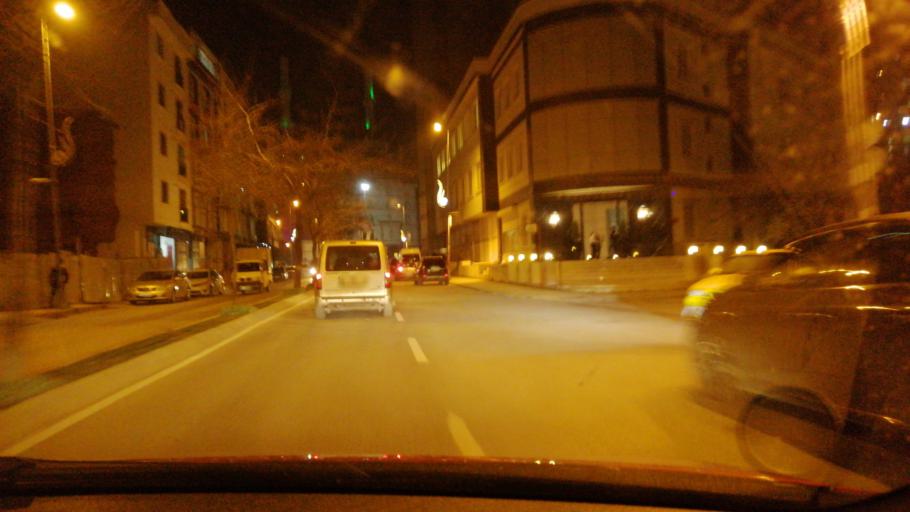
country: TR
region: Istanbul
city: Sisli
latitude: 41.0855
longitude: 28.9735
